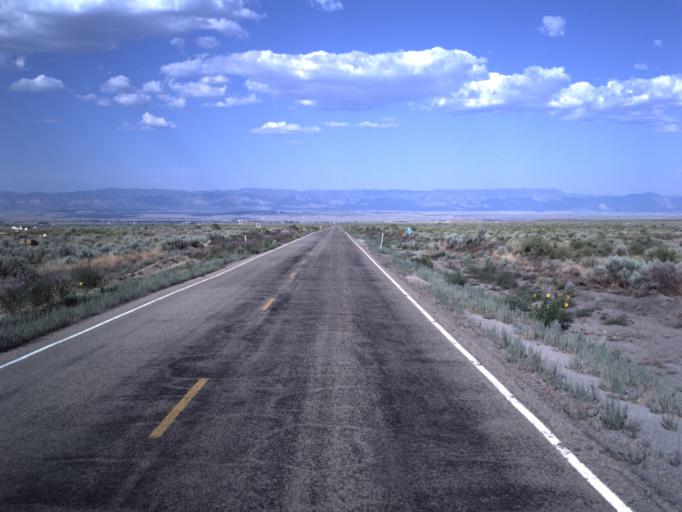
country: US
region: Utah
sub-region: Carbon County
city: Price
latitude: 39.4864
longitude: -110.8783
